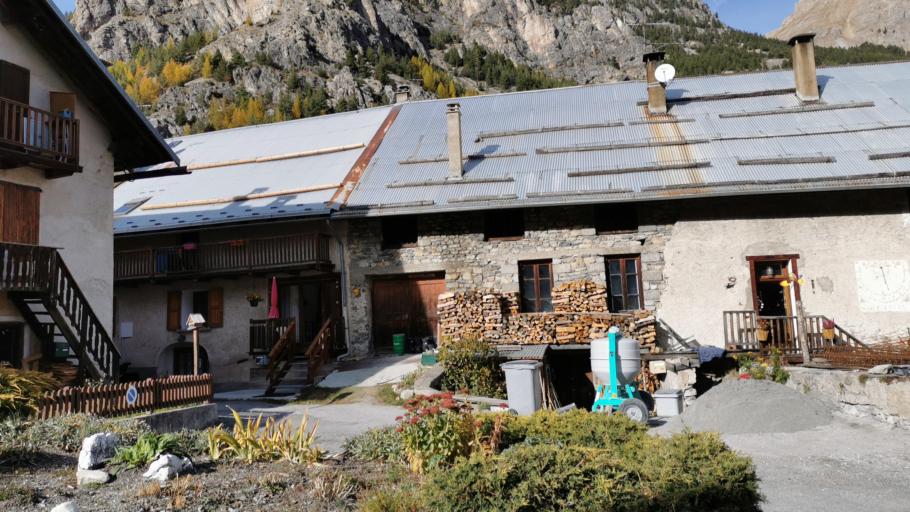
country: FR
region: Provence-Alpes-Cote d'Azur
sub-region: Departement des Hautes-Alpes
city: Villeneuve
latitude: 45.0186
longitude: 6.6044
